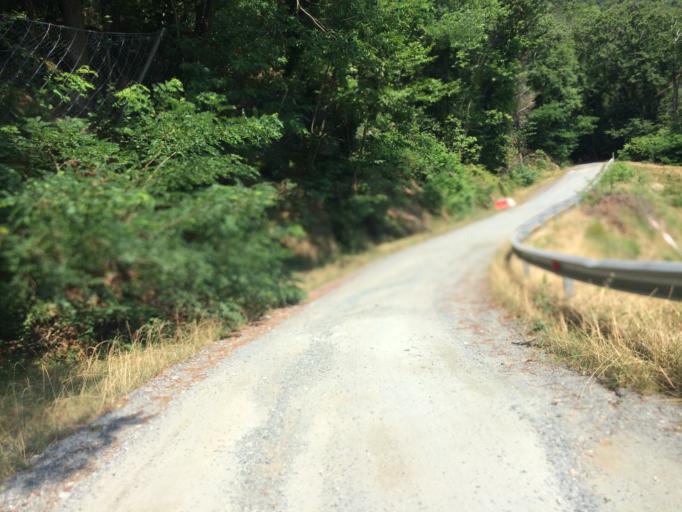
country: IT
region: Liguria
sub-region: Provincia di Genova
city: Sciarborasca
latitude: 44.4031
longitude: 8.5744
